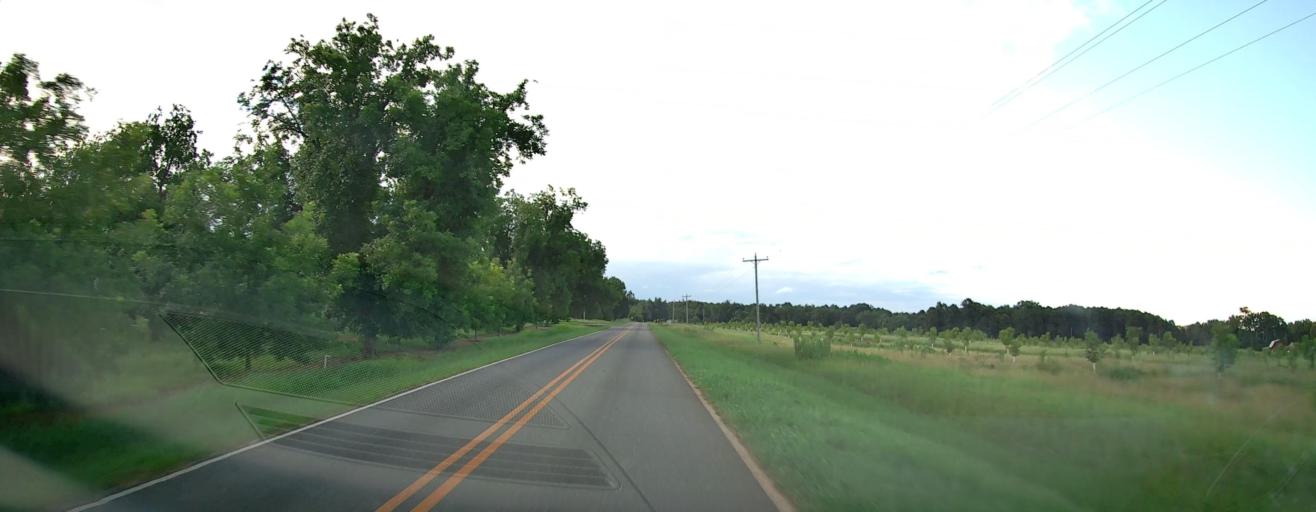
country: US
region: Georgia
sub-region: Pulaski County
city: Hawkinsville
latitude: 32.3182
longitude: -83.5522
